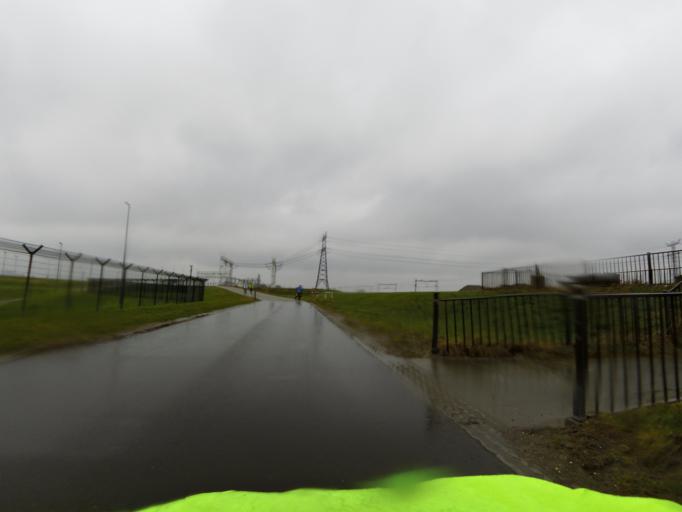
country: NL
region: South Holland
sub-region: Gemeente Rotterdam
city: Hoek van Holland
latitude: 51.9577
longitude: 4.1672
